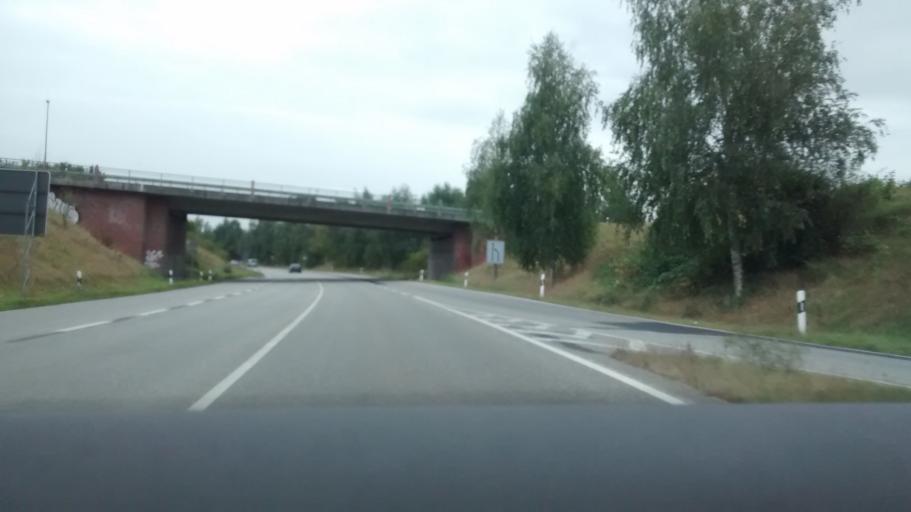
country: DE
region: Mecklenburg-Vorpommern
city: Wismar
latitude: 53.8779
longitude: 11.4228
